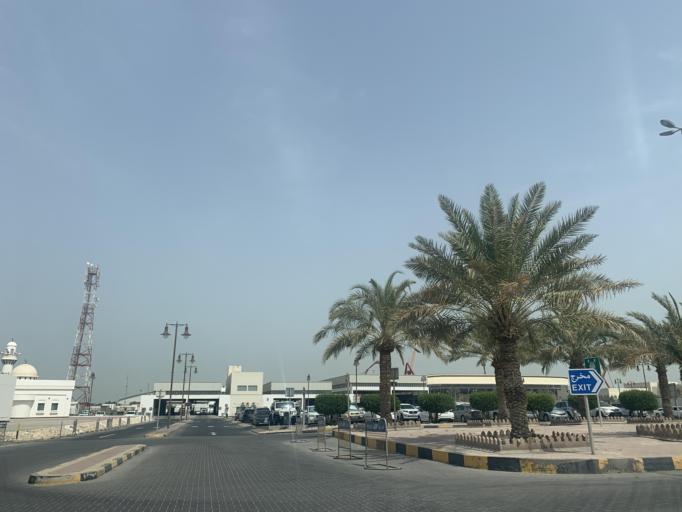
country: BH
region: Northern
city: Madinat `Isa
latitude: 26.1559
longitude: 50.5383
